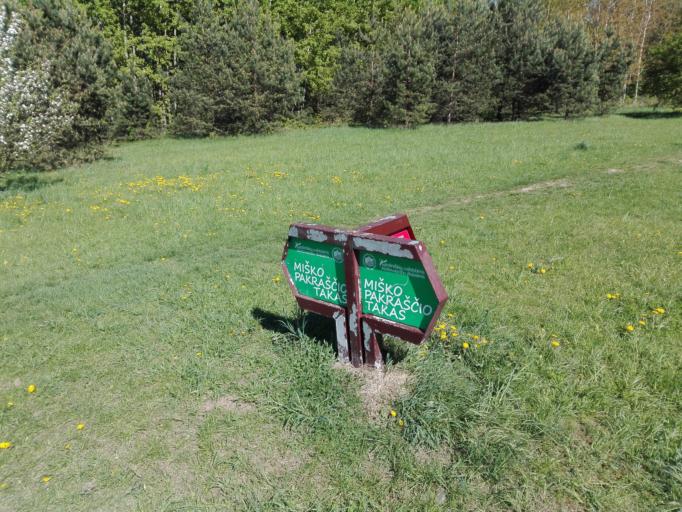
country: LT
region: Vilnius County
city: Lazdynai
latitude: 54.6883
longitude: 25.2188
